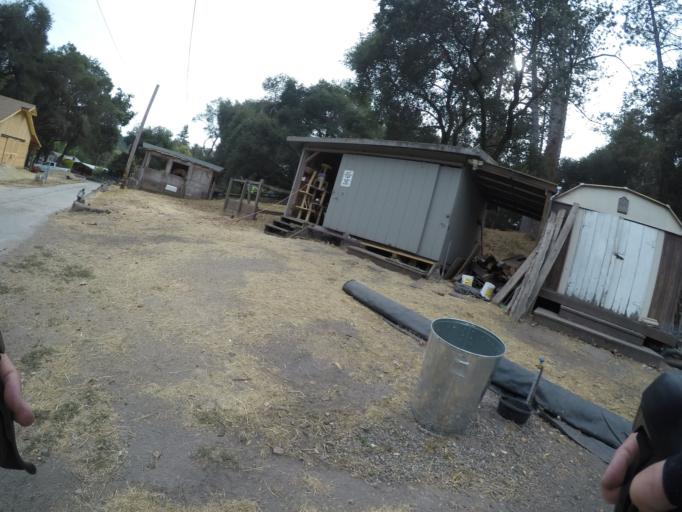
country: US
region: California
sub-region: Santa Cruz County
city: Mount Hermon
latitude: 37.0722
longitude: -122.0584
